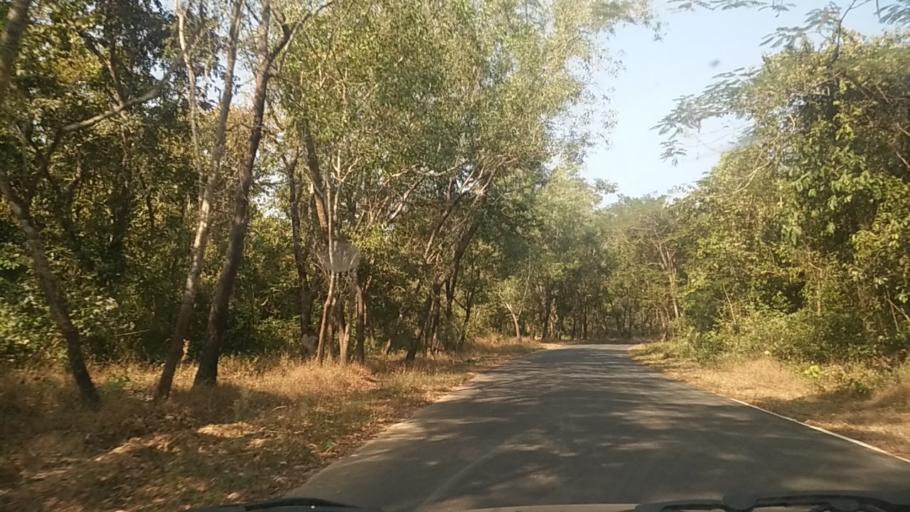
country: IN
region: Goa
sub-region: South Goa
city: Sanguem
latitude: 15.2021
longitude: 74.2231
